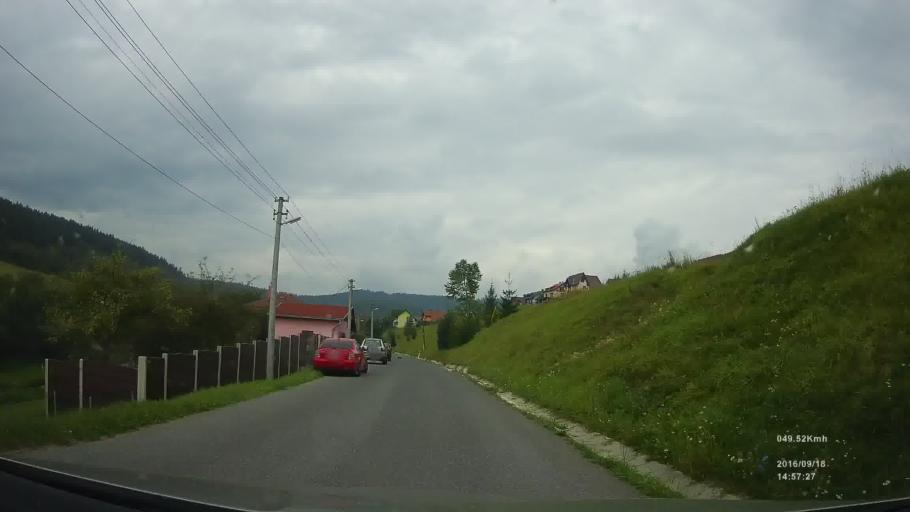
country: SK
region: Presovsky
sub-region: Okres Presov
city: Levoca
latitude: 49.0222
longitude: 20.5245
